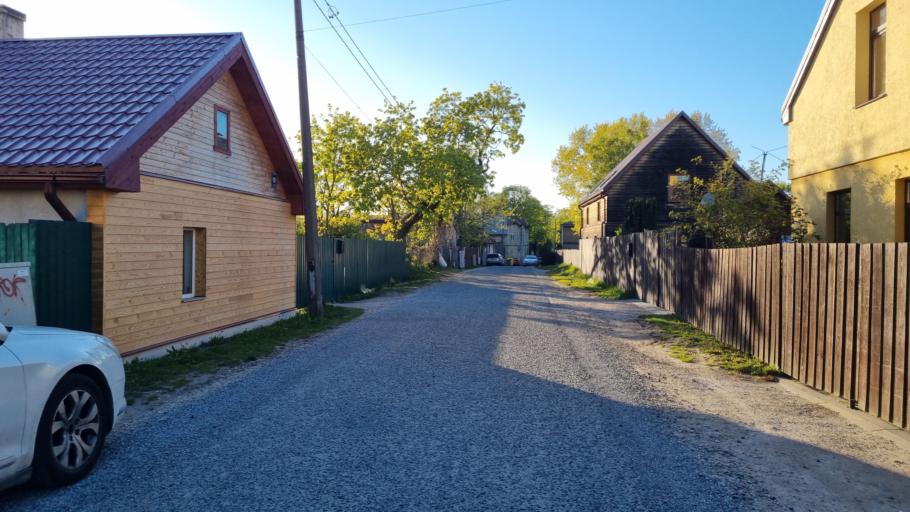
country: LV
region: Riga
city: Bolderaja
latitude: 57.0341
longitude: 24.0450
